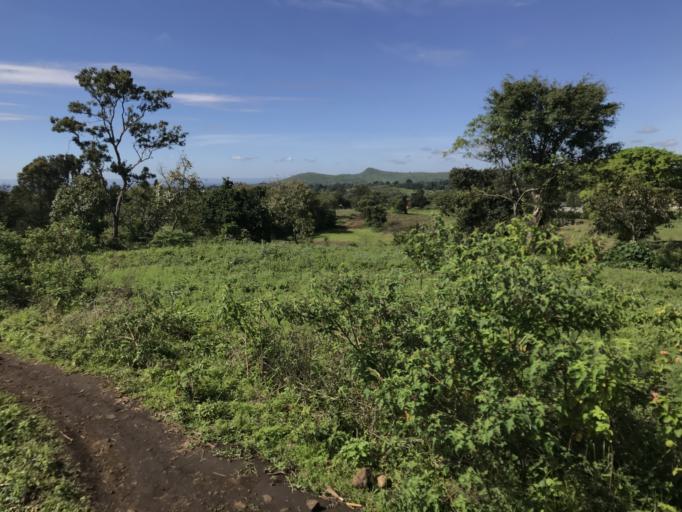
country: TZ
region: Arusha
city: Usa River
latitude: -3.3944
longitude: 36.7970
